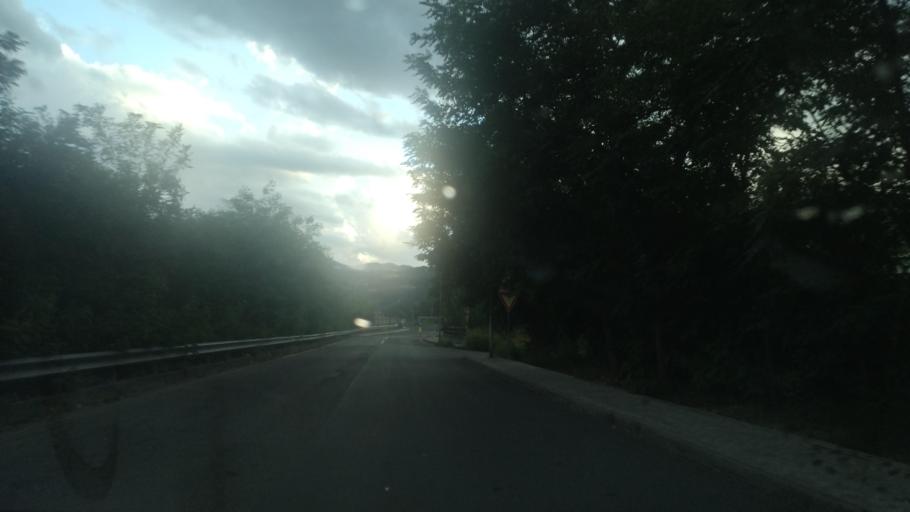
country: IT
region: Calabria
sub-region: Provincia di Catanzaro
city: Montepaone Lido
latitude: 38.7287
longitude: 16.5362
